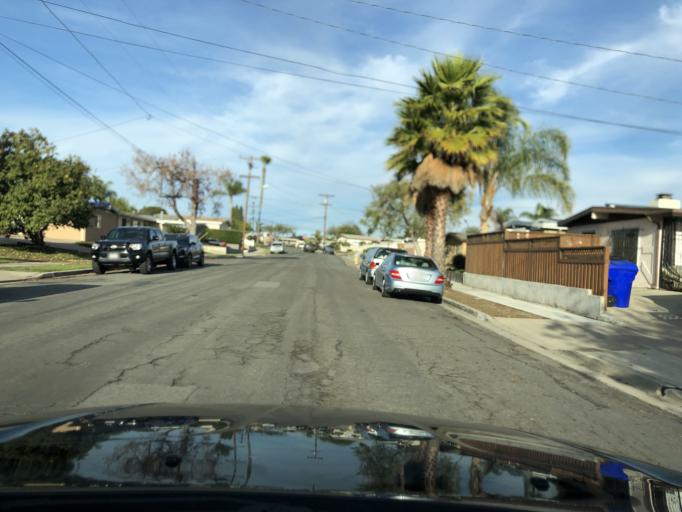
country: US
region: California
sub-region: San Diego County
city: La Jolla
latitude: 32.8260
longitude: -117.1772
